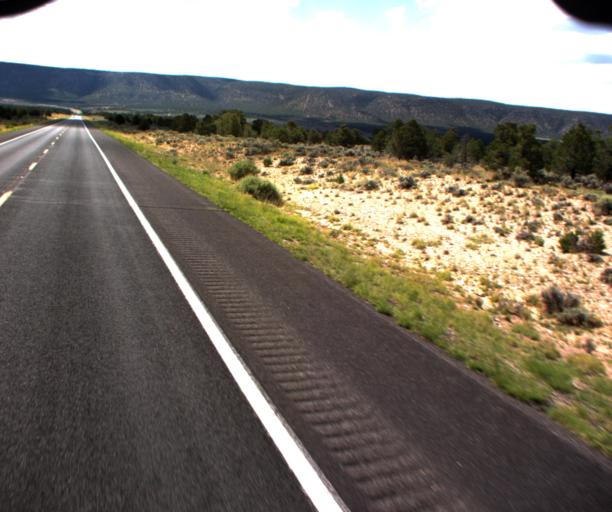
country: US
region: Arizona
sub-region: Coconino County
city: Grand Canyon
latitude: 35.9460
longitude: -111.7784
